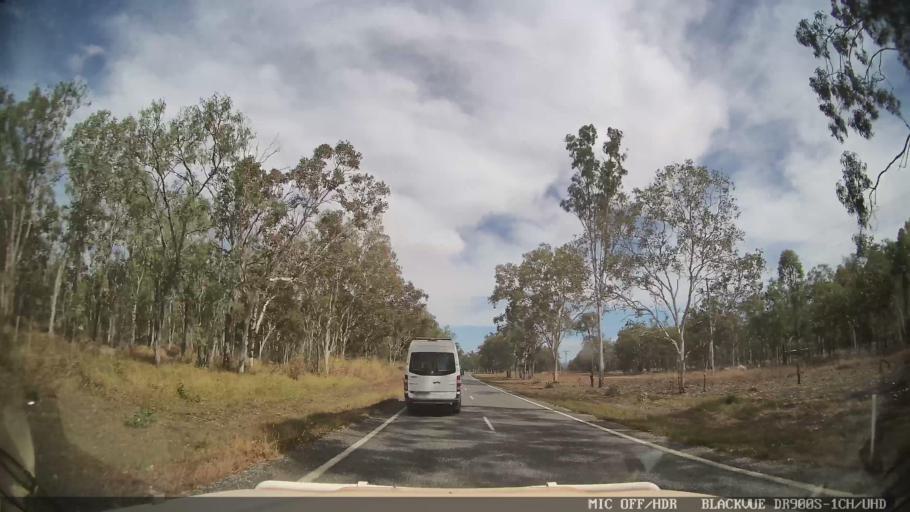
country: AU
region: Queensland
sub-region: Cairns
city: Port Douglas
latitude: -16.7269
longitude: 145.3526
